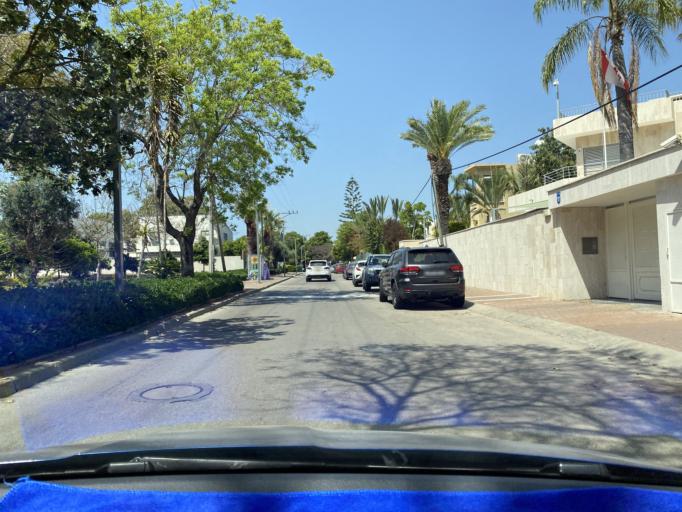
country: IL
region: Tel Aviv
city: Kefar Shemaryahu
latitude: 32.1783
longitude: 34.8147
